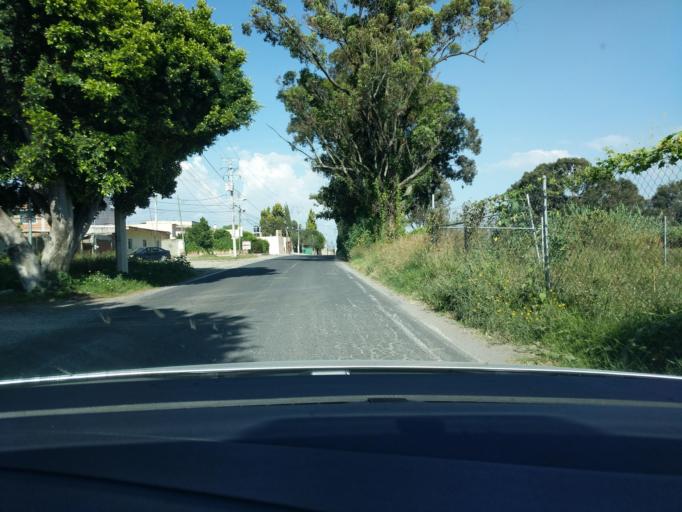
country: MX
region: Puebla
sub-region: Ocoyucan
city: San Bernabe Temoxtitla
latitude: 19.0008
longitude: -98.3427
